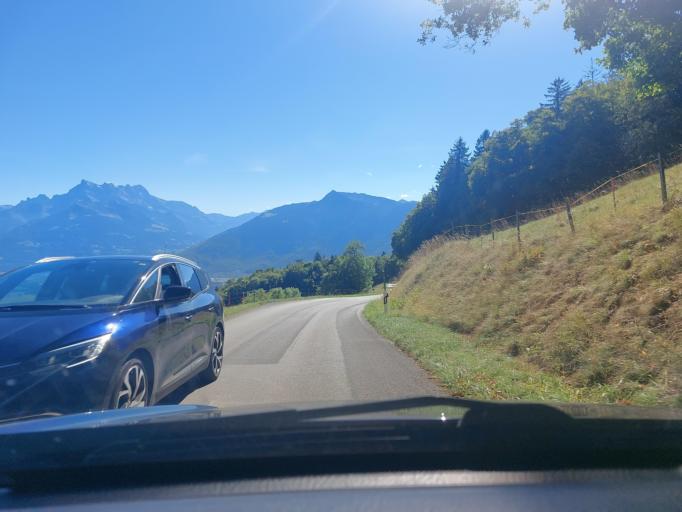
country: CH
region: Vaud
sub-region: Aigle District
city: Aigle
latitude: 46.3434
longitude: 6.9585
